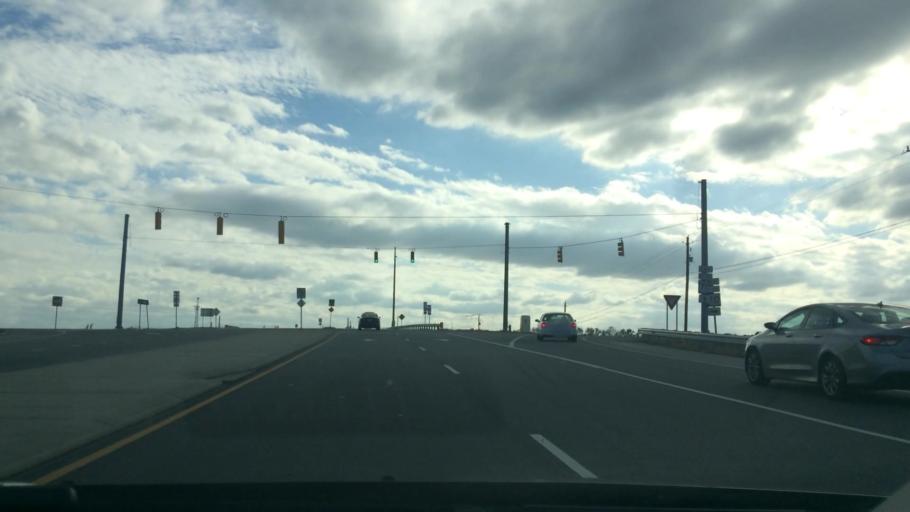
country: US
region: North Carolina
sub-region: Wayne County
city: Elroy
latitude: 35.4138
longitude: -77.8968
